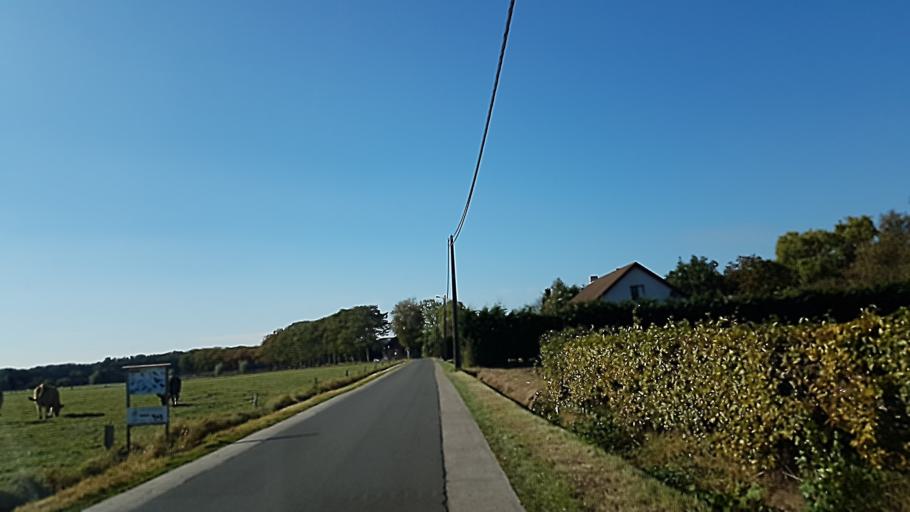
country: BE
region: Flanders
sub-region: Provincie Antwerpen
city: Essen
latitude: 51.4354
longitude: 4.3982
